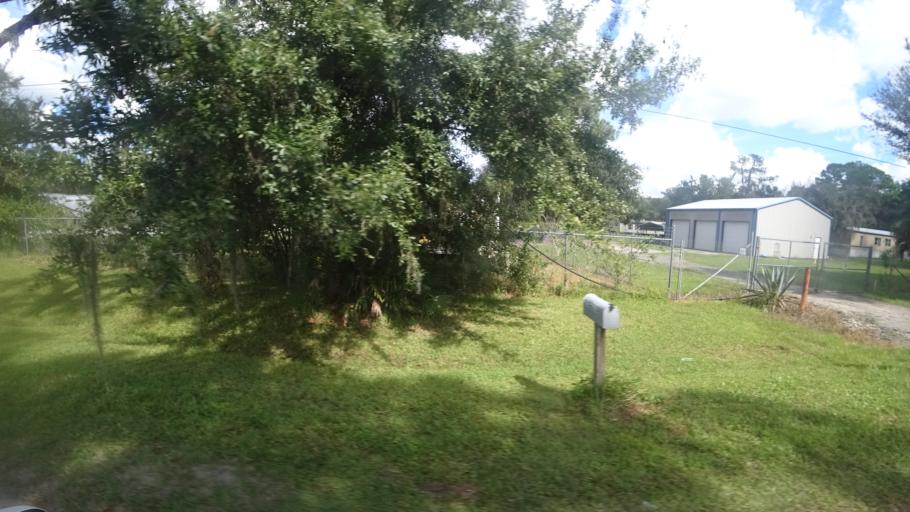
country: US
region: Florida
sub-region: Hillsborough County
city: Sun City Center
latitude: 27.6497
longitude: -82.3763
